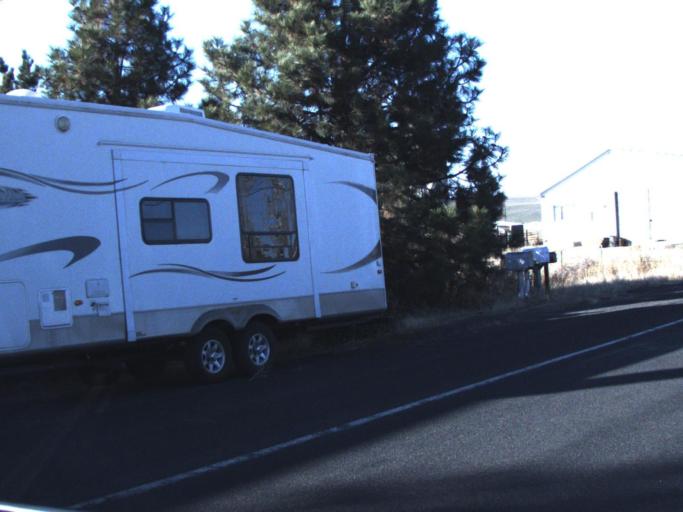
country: US
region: Washington
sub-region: Adams County
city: Ritzville
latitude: 46.9836
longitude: -118.3434
